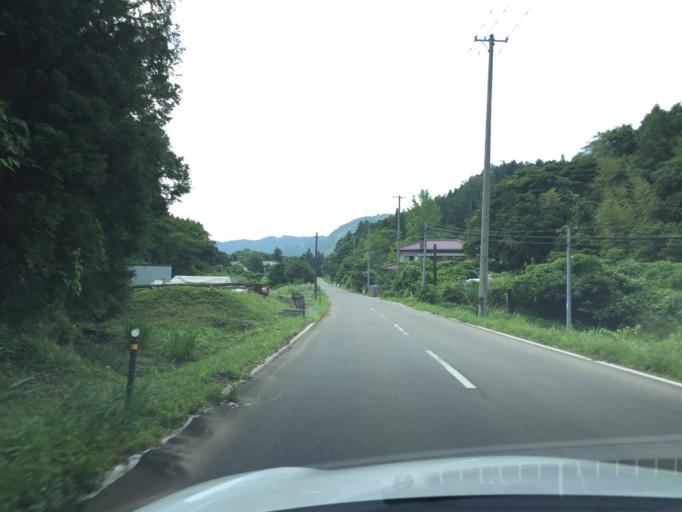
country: JP
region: Fukushima
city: Iwaki
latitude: 37.0551
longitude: 140.6931
